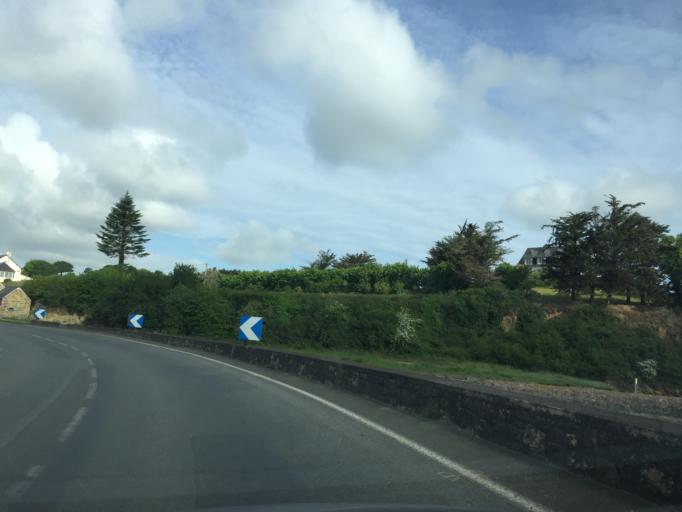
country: FR
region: Brittany
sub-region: Departement des Cotes-d'Armor
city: Matignon
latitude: 48.6134
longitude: -2.3200
